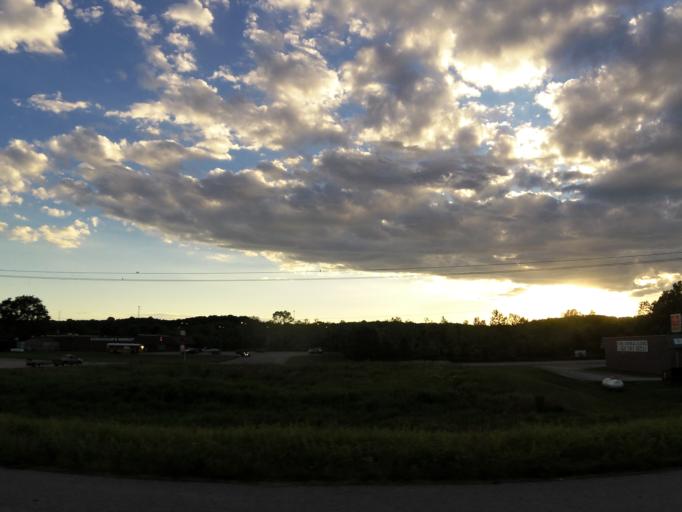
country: US
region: Missouri
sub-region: Jefferson County
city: Cedar Hill
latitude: 38.3522
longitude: -90.6495
